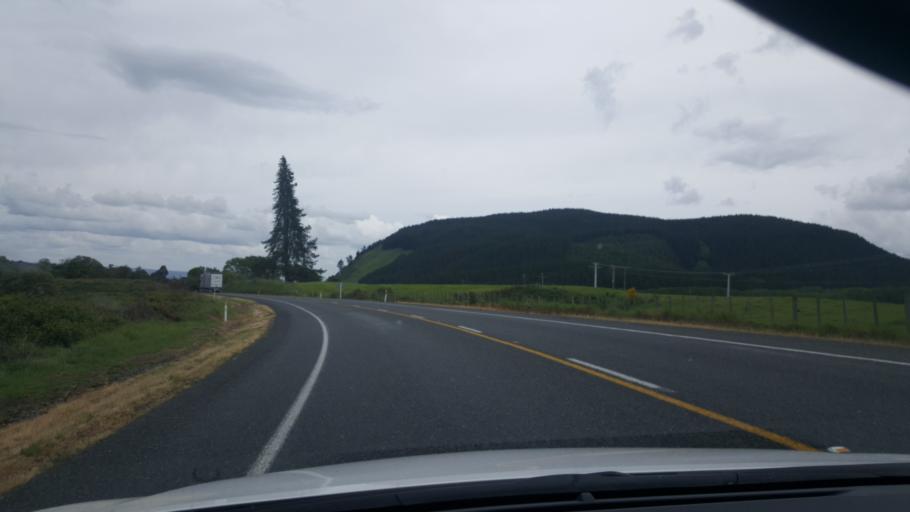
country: NZ
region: Bay of Plenty
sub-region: Rotorua District
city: Rotorua
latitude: -38.3432
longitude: 176.3612
